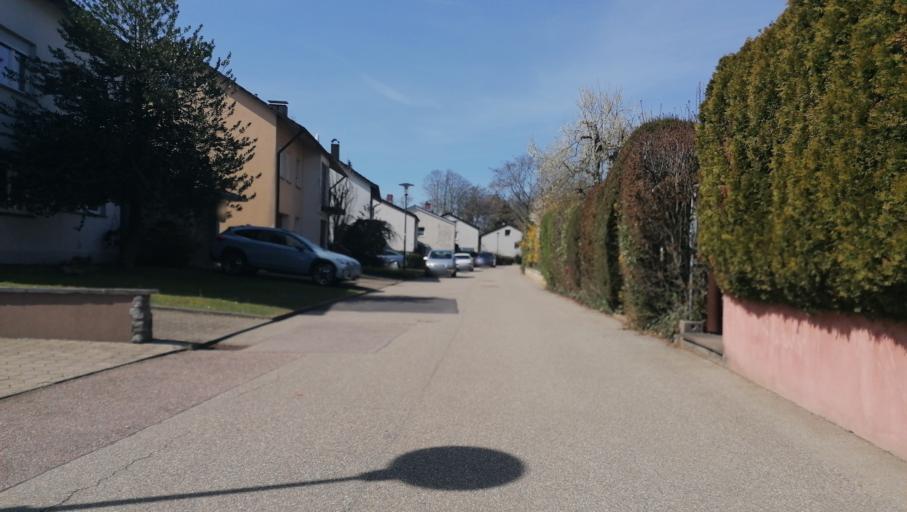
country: DE
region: Baden-Wuerttemberg
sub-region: Freiburg Region
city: Bad Sackingen
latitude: 47.5600
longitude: 7.9307
